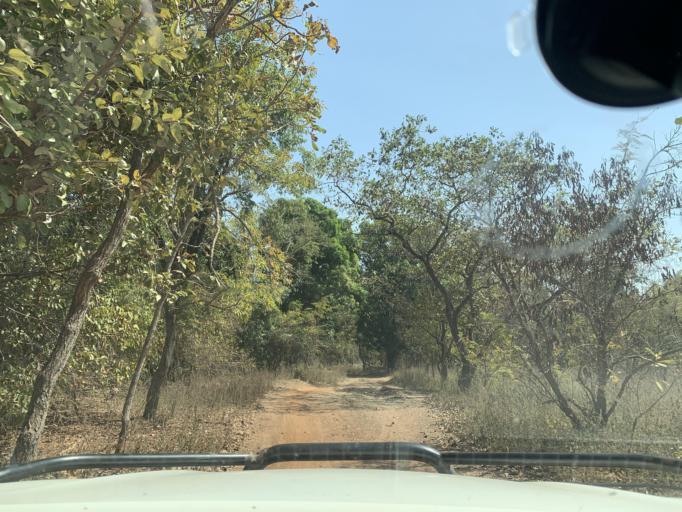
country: ML
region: Sikasso
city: Kolondieba
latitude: 10.8297
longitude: -6.7269
